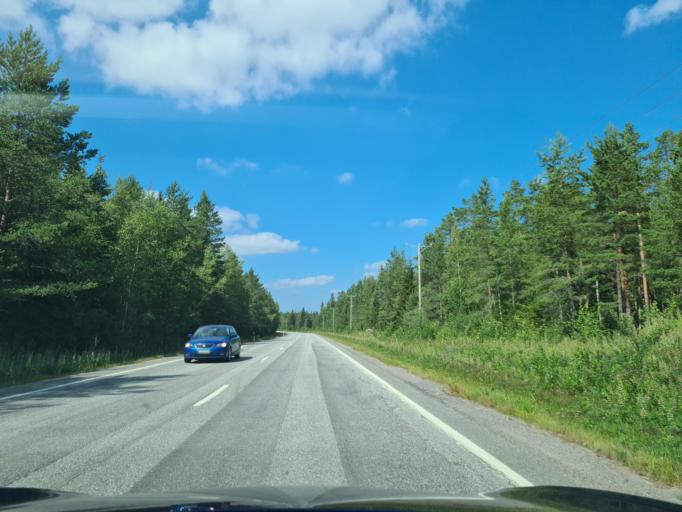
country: FI
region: Ostrobothnia
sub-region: Vaasa
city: Vaasa
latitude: 63.1760
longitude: 21.5774
